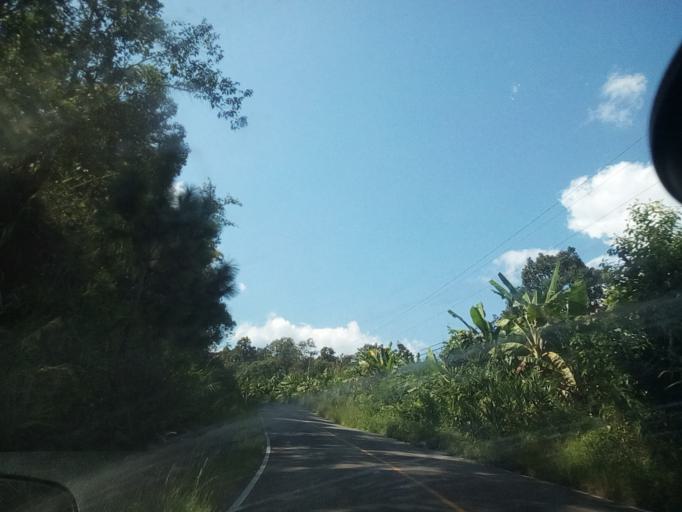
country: TH
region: Chiang Mai
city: Samoeng
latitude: 18.8640
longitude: 98.7012
